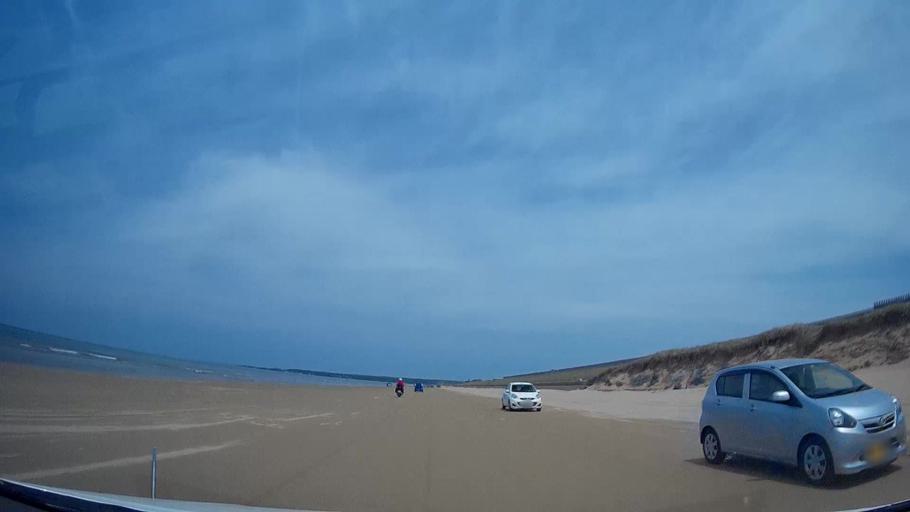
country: JP
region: Ishikawa
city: Hakui
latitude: 36.8753
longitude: 136.7612
